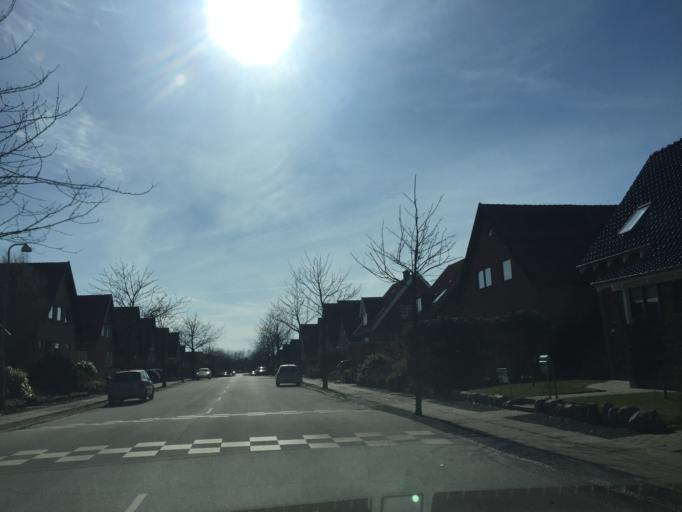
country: DK
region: South Denmark
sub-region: Odense Kommune
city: Odense
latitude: 55.3901
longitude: 10.4193
